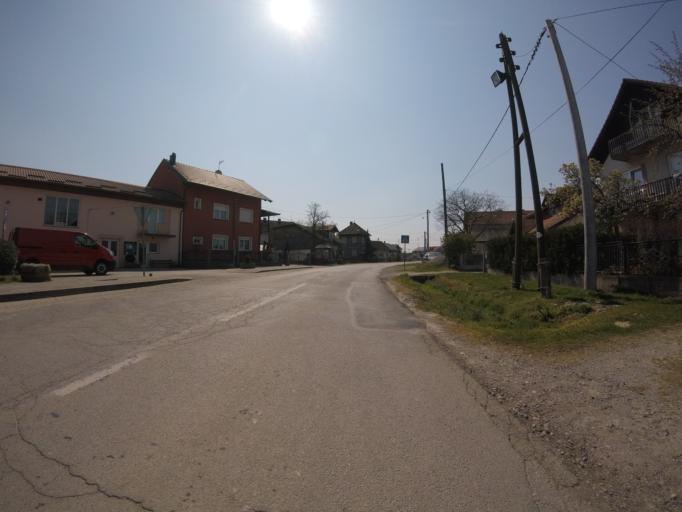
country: HR
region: Zagrebacka
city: Lukavec
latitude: 45.7049
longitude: 15.9897
